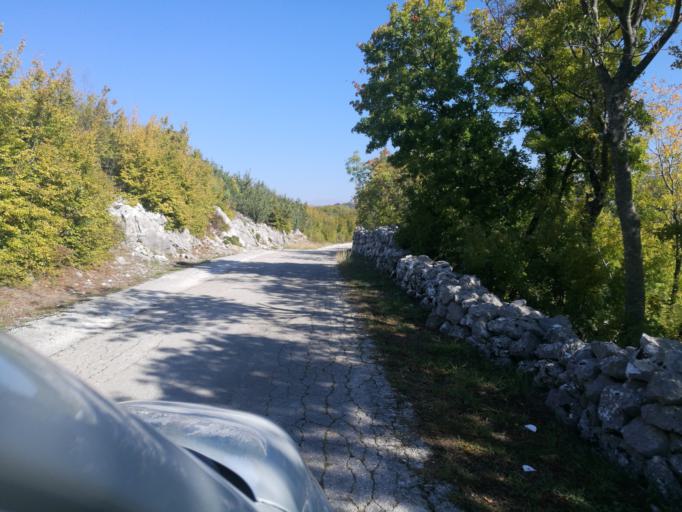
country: HR
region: Splitsko-Dalmatinska
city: Trilj
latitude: 43.5408
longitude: 16.7327
